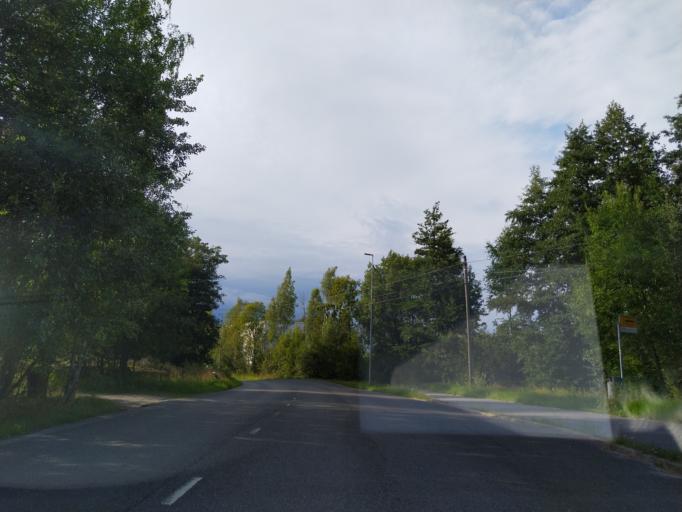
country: FI
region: Varsinais-Suomi
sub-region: Turku
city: Turku
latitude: 60.4288
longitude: 22.2241
